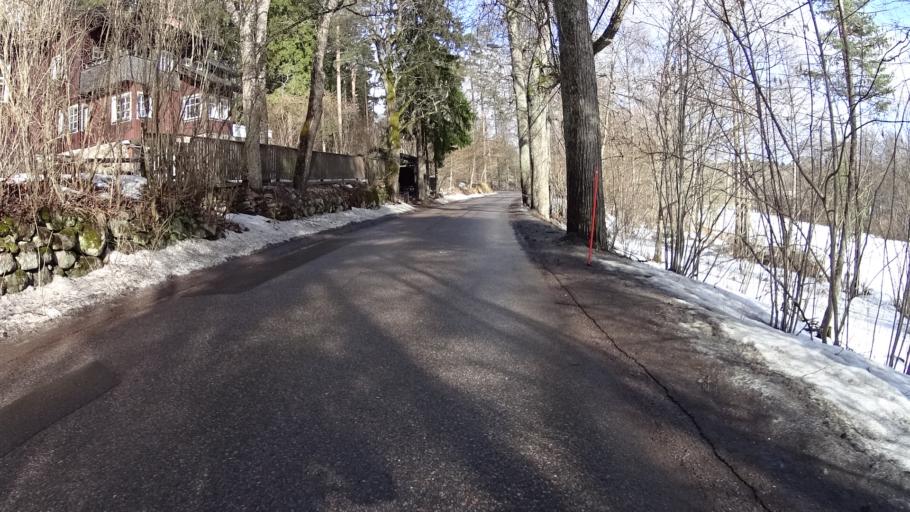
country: FI
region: Uusimaa
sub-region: Helsinki
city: Espoo
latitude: 60.2694
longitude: 24.6539
